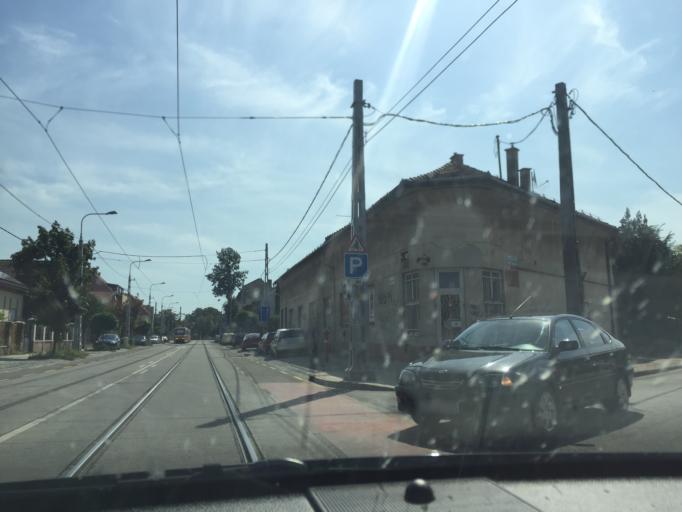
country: HU
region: Budapest
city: Budapest XV. keruelet
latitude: 47.5654
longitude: 19.1074
